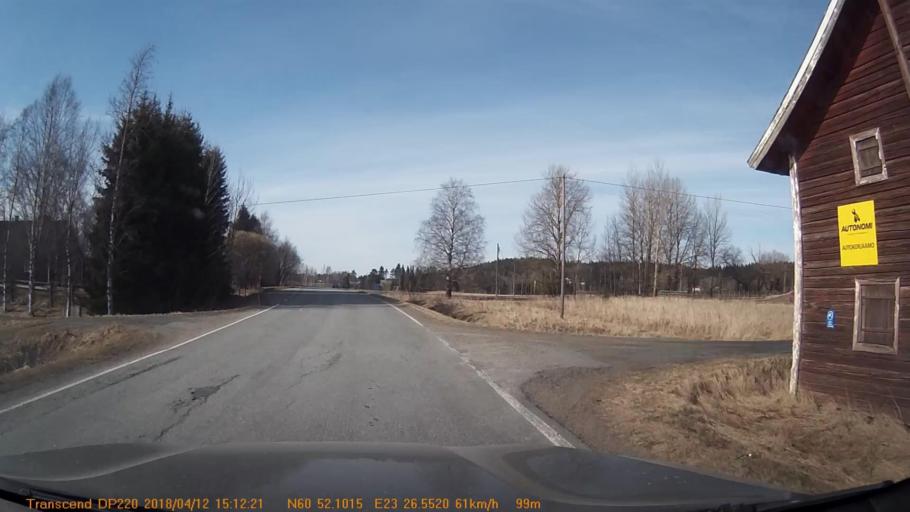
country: FI
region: Haeme
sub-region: Forssa
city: Jokioinen
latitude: 60.8684
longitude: 23.4425
